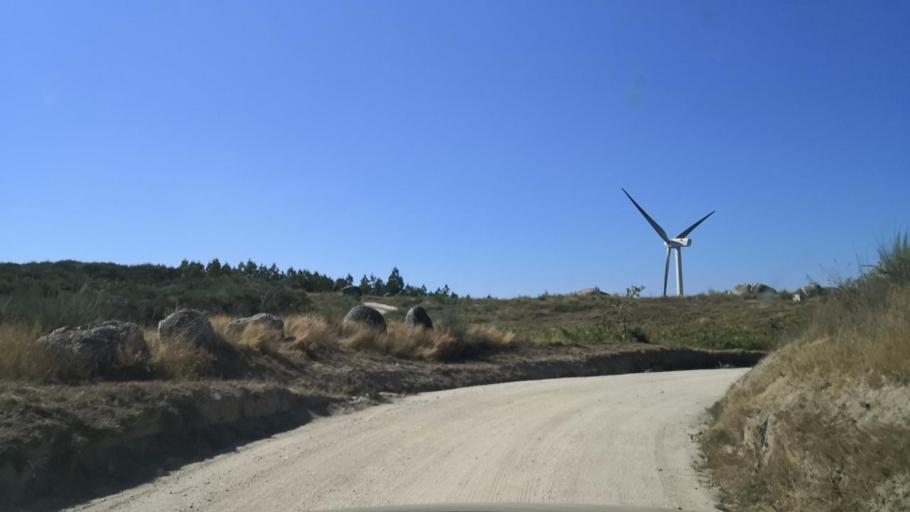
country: PT
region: Braga
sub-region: Cabeceiras de Basto
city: Refojos de Basto
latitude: 41.4901
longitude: -8.0695
